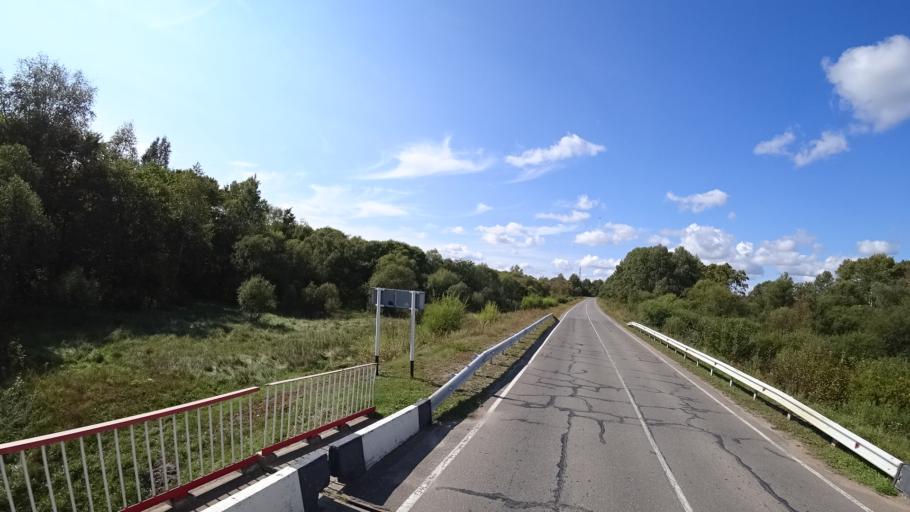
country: RU
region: Amur
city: Arkhara
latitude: 49.4063
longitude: 130.1237
